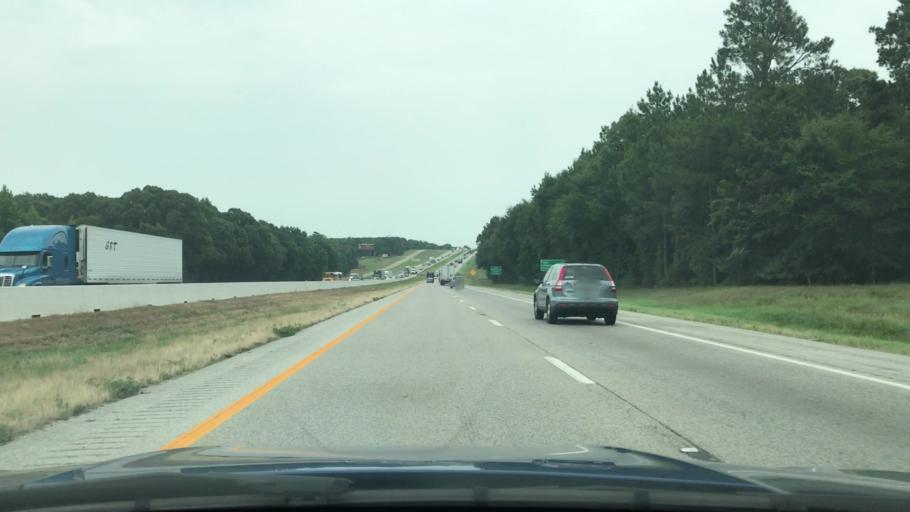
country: US
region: Texas
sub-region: Van Zandt County
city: Van
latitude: 32.4962
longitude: -95.5728
